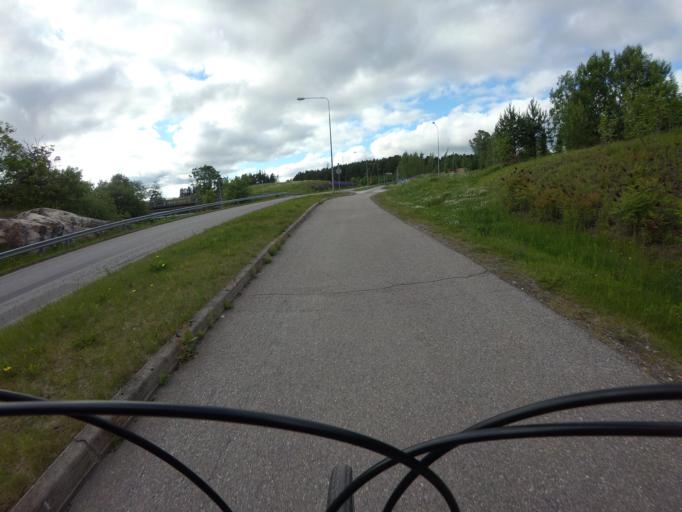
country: FI
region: Varsinais-Suomi
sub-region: Turku
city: Vahto
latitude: 60.5366
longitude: 22.3452
